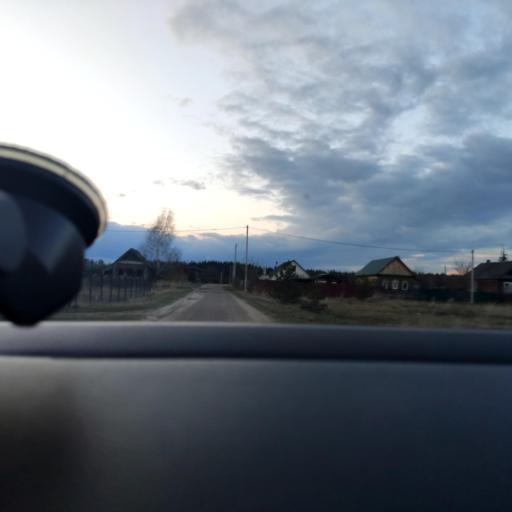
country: RU
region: Moskovskaya
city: Shaturtorf
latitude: 55.4336
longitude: 39.4276
